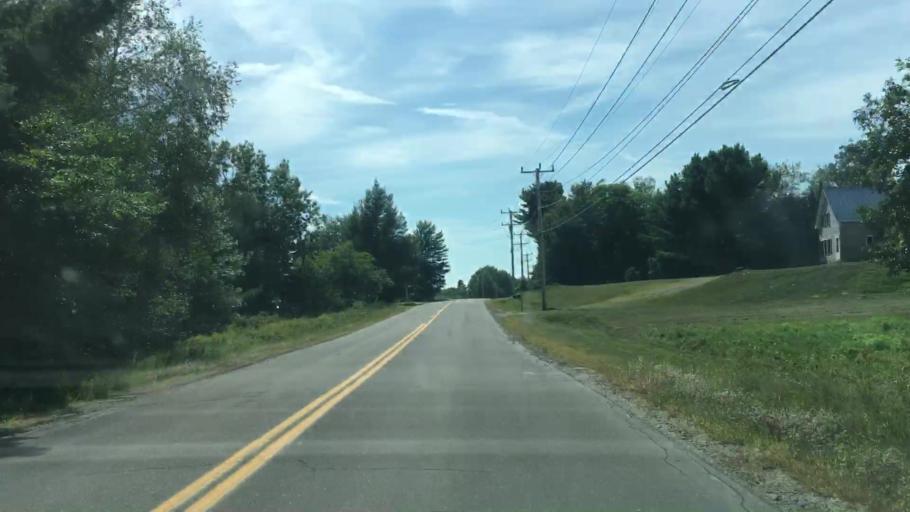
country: US
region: Maine
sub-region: Penobscot County
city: Lincoln
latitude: 45.4345
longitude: -68.4632
